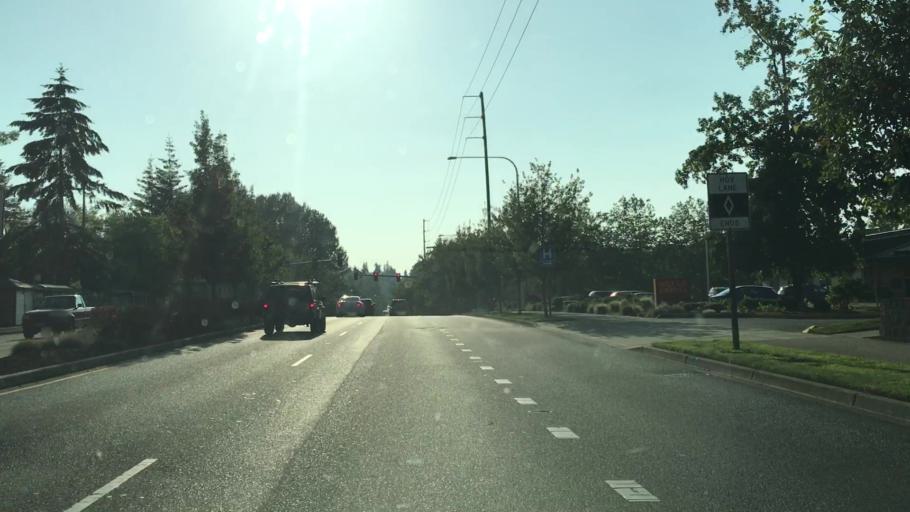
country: US
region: Washington
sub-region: King County
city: Federal Way
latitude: 47.2899
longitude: -122.3215
